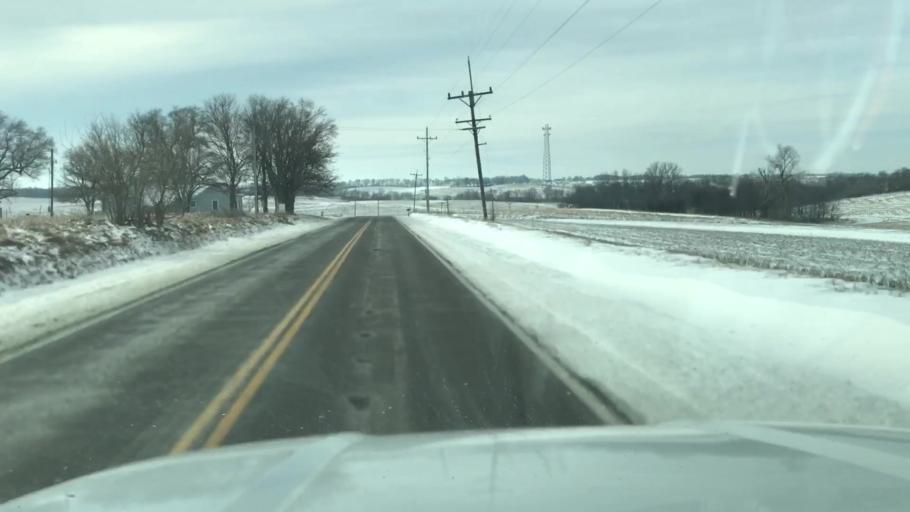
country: US
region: Missouri
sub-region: Holt County
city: Oregon
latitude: 40.0516
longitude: -95.1357
